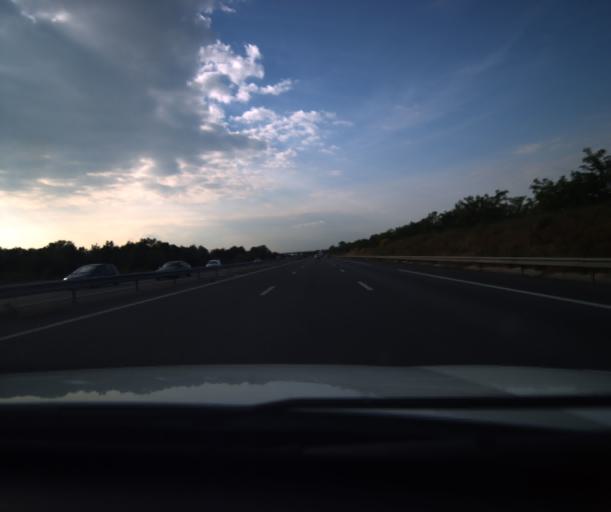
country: FR
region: Midi-Pyrenees
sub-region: Departement du Tarn-et-Garonne
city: Pompignan
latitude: 43.8273
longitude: 1.3439
